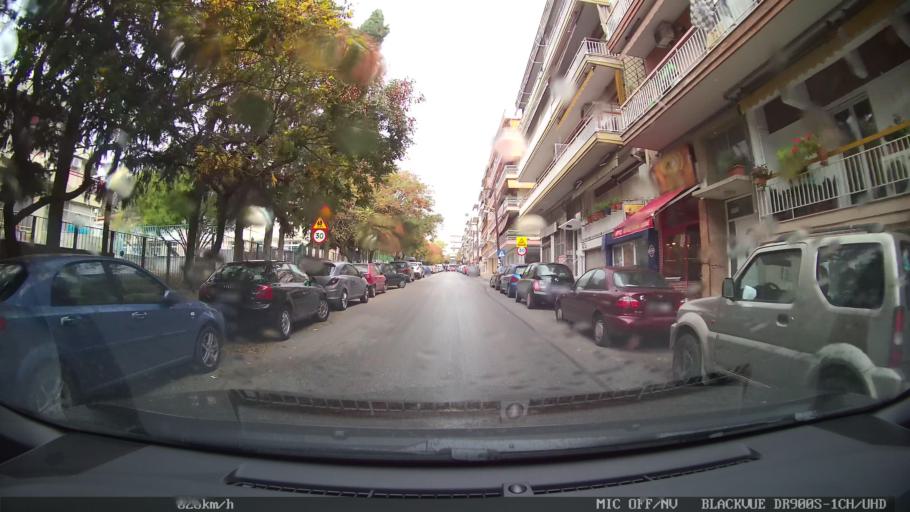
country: GR
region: Central Macedonia
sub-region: Nomos Thessalonikis
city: Triandria
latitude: 40.6116
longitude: 22.9801
